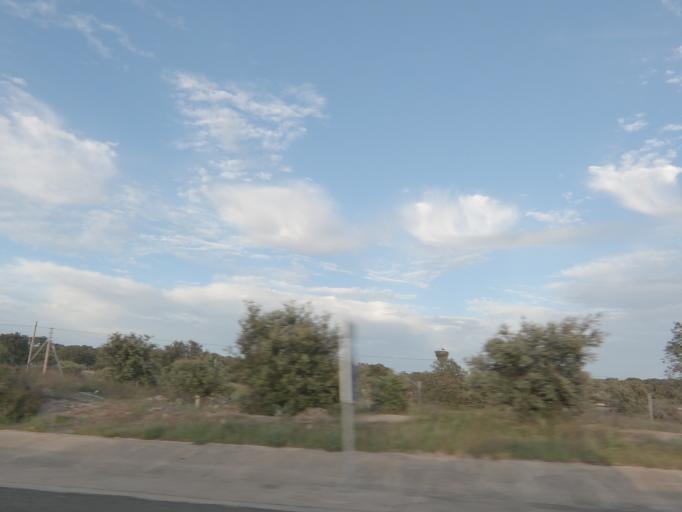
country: ES
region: Extremadura
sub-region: Provincia de Badajoz
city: Mirandilla
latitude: 38.9918
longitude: -6.3294
